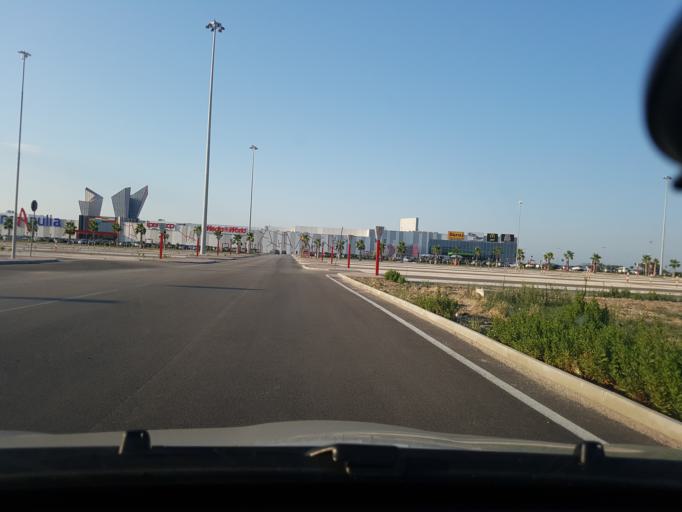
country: IT
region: Apulia
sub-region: Provincia di Foggia
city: Carapelle
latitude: 41.4132
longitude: 15.6515
